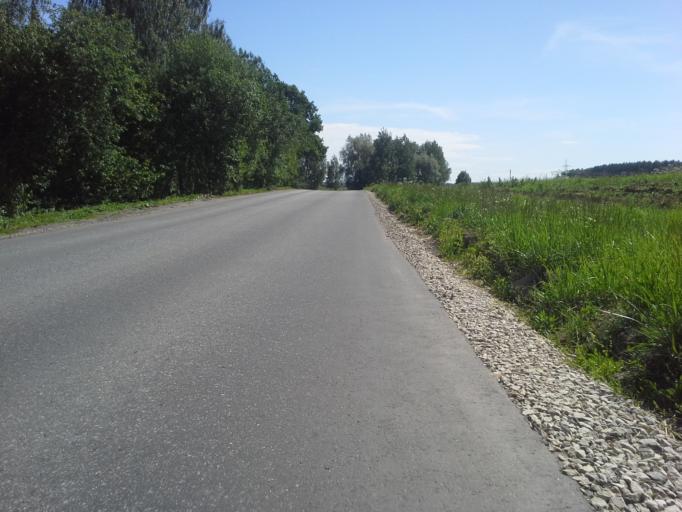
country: RU
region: Moskovskaya
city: Dubrovitsy
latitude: 55.4859
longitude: 37.4427
